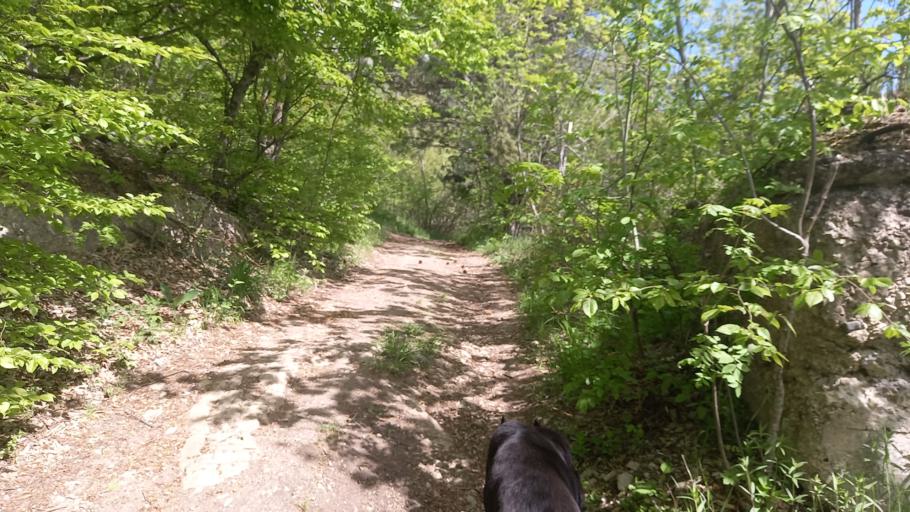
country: RU
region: Stavropol'skiy
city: Pyatigorsk
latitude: 44.0878
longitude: 43.0295
